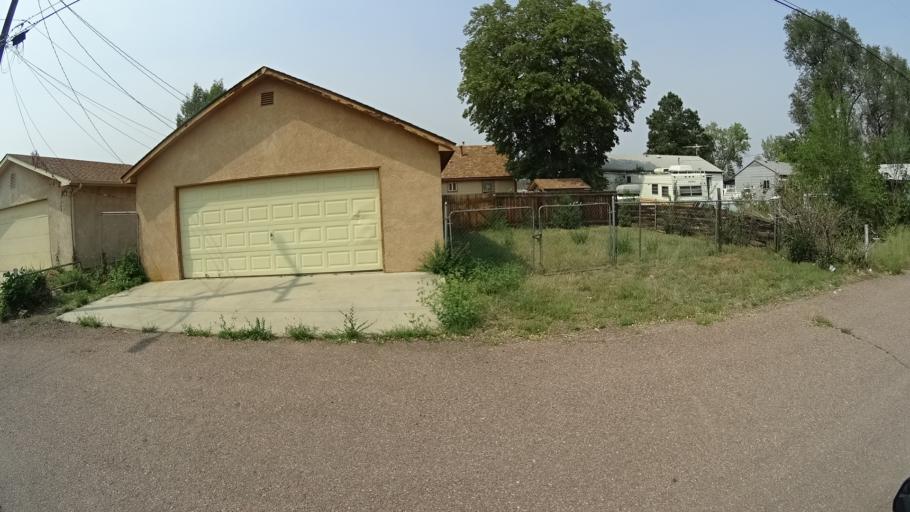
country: US
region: Colorado
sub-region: El Paso County
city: Colorado Springs
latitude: 38.8098
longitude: -104.8184
